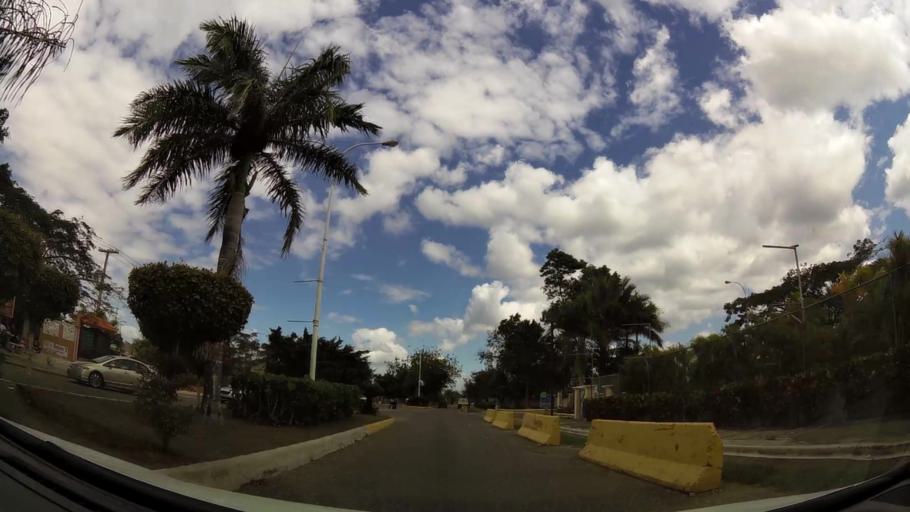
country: DO
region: Santo Domingo
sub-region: Santo Domingo
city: Boca Chica
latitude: 18.4525
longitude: -69.6632
